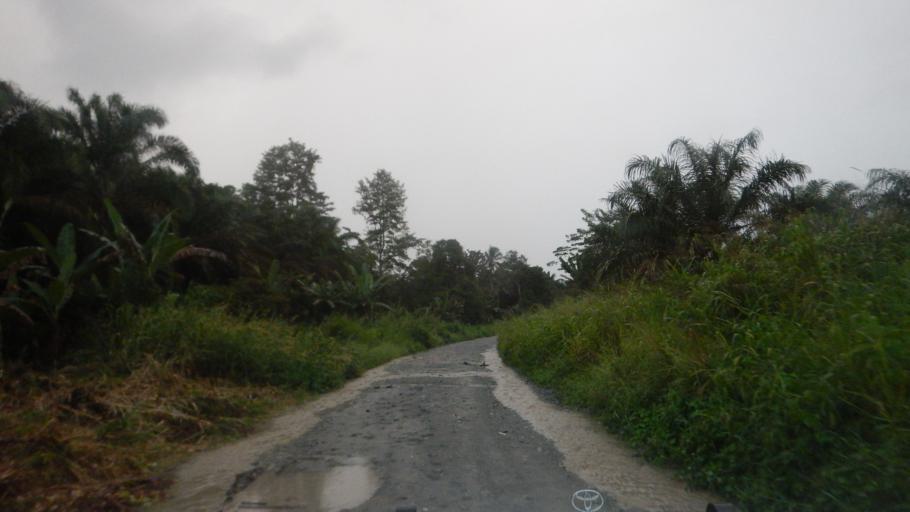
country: PG
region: Northern Province
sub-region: Sohe
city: Kokoda
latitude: -8.9129
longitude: 147.9566
